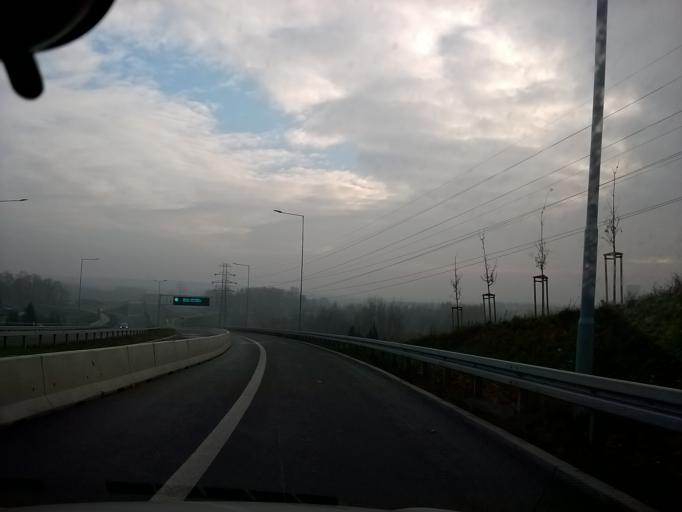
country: PL
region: Silesian Voivodeship
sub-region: Ruda Slaska
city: Ruda Slaska
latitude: 50.2771
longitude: 18.8452
